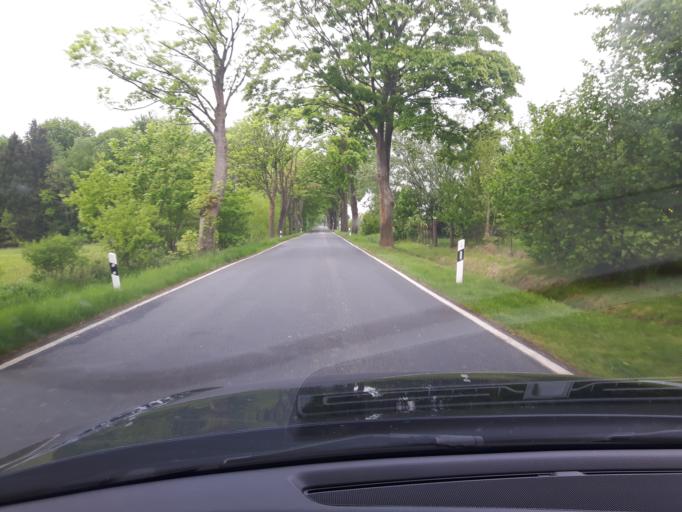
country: DE
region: Mecklenburg-Vorpommern
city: Tribsees
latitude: 54.1778
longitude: 12.7403
